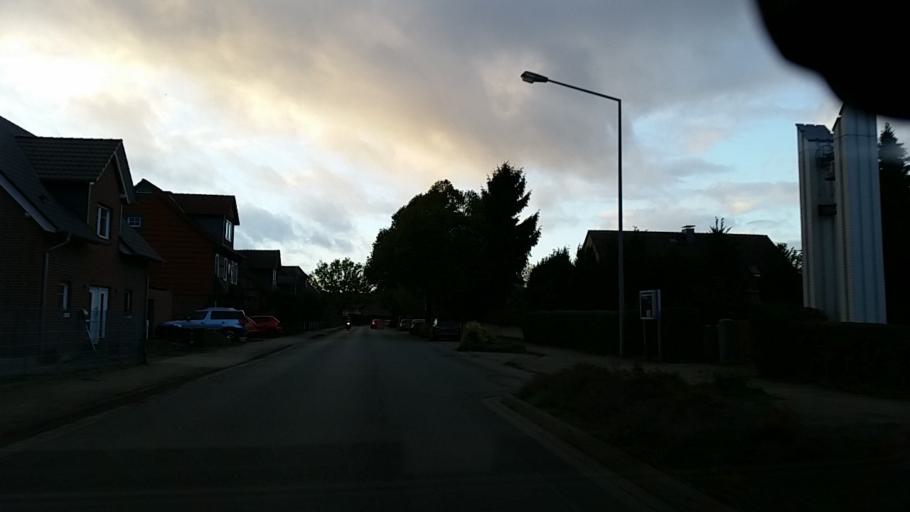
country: DE
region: Lower Saxony
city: Tappenbeck
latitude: 52.4550
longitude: 10.7526
